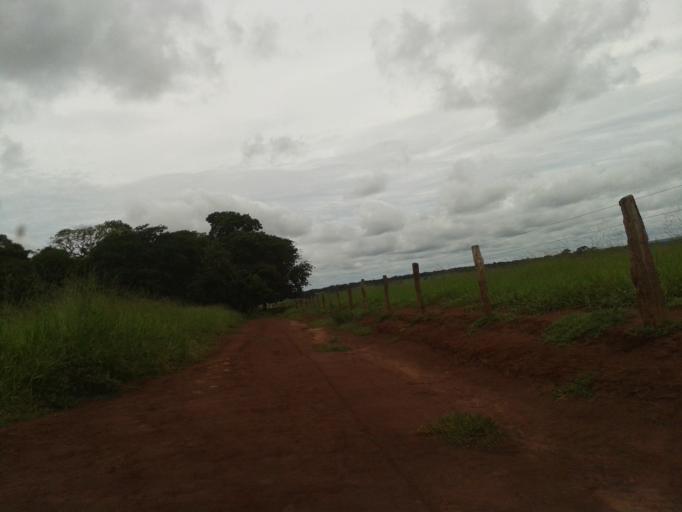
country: BR
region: Minas Gerais
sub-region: Capinopolis
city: Capinopolis
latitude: -18.7860
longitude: -49.7811
